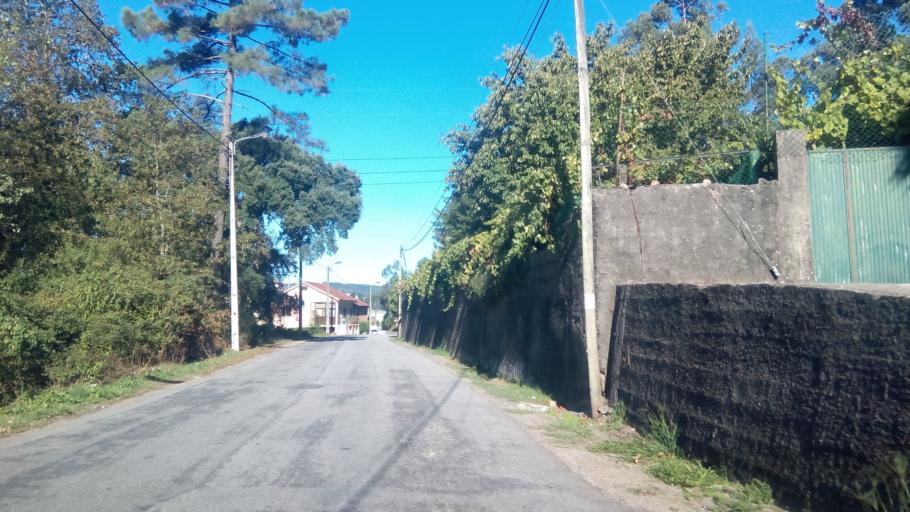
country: PT
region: Porto
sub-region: Paredes
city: Gandra
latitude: 41.1873
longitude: -8.4400
